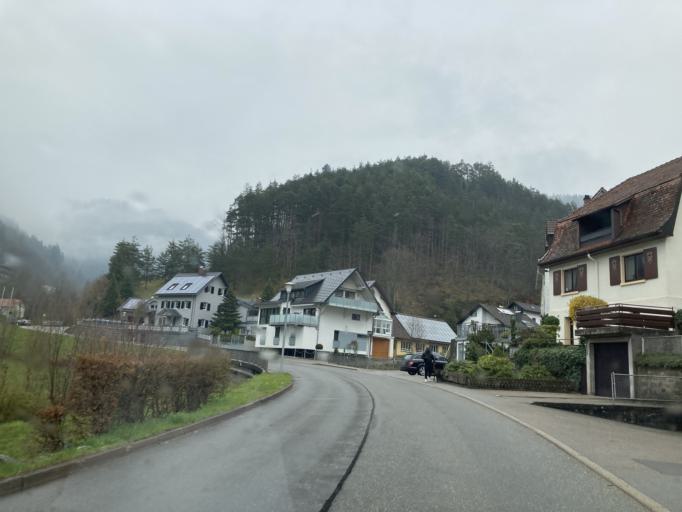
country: DE
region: Baden-Wuerttemberg
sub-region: Freiburg Region
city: Hornberg
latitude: 48.2158
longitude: 8.2403
